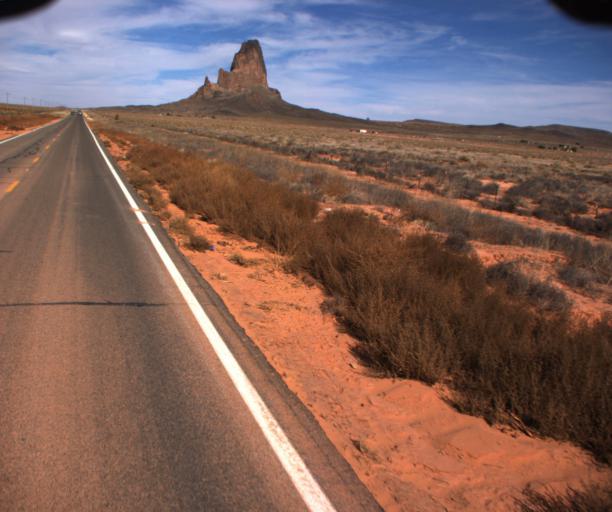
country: US
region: Arizona
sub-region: Navajo County
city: Kayenta
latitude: 36.7954
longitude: -110.2315
